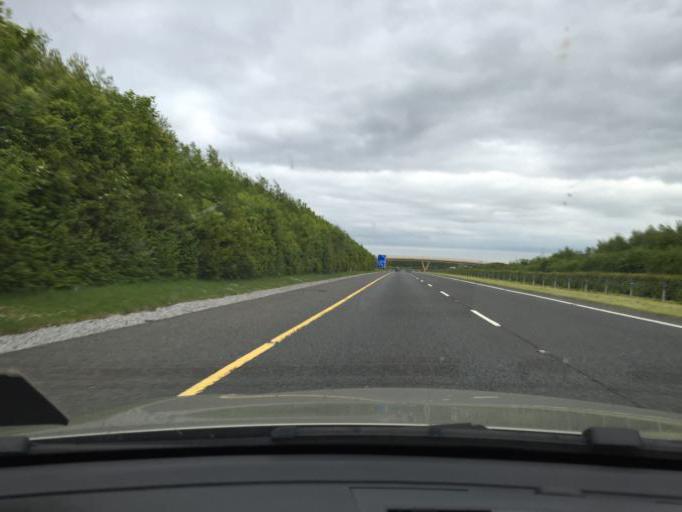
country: IE
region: Leinster
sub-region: An Mhi
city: Stamullin
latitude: 53.6471
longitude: -6.2715
